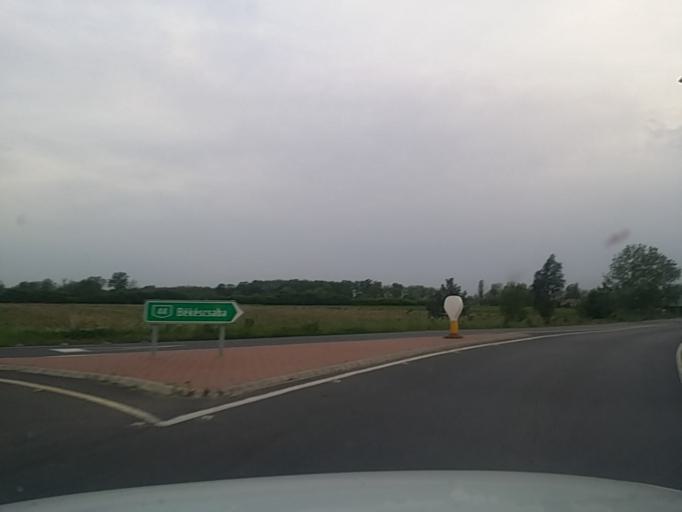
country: HU
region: Bekes
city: Gyula
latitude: 46.6305
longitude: 21.2981
